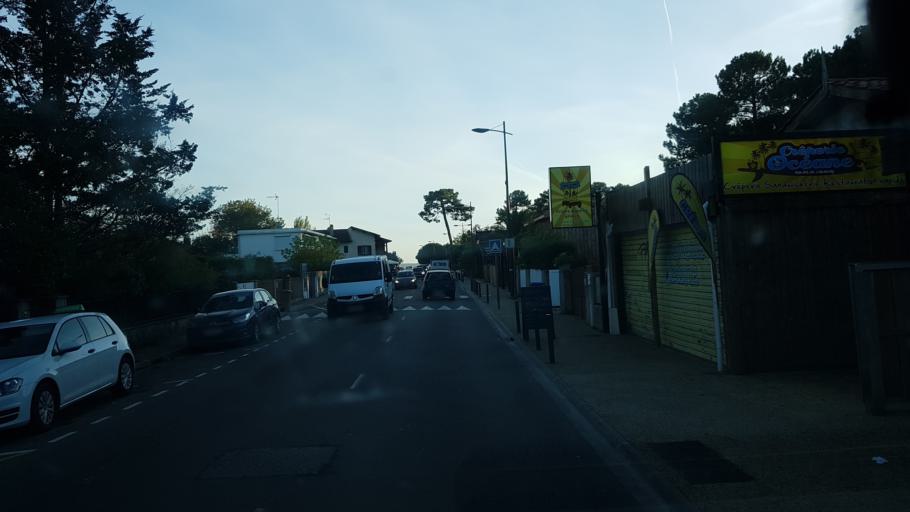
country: FR
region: Aquitaine
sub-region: Departement de la Gironde
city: Ares
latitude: 44.7464
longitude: -1.1812
